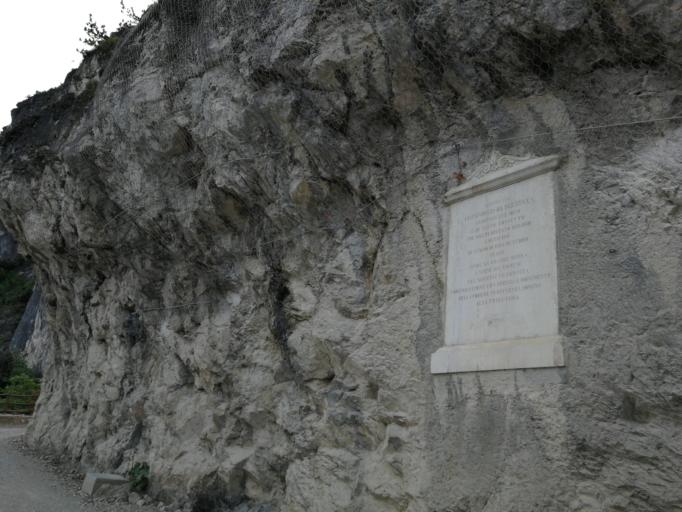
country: IT
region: Trentino-Alto Adige
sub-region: Provincia di Trento
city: Riva del Garda
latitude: 45.8766
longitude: 10.8387
